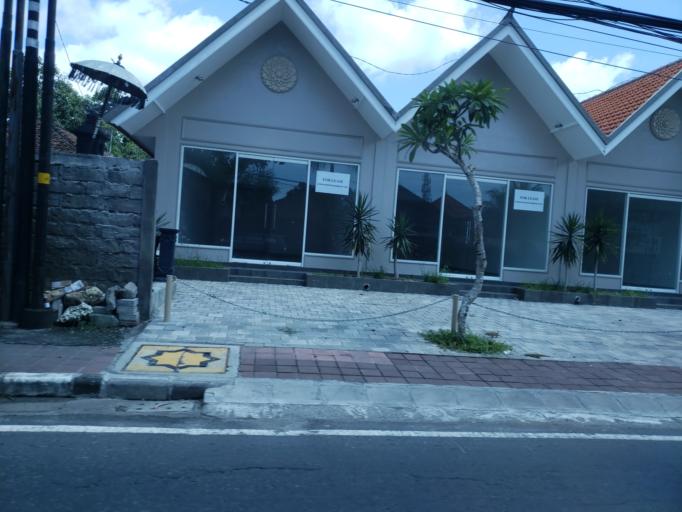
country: ID
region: Bali
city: Jimbaran
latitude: -8.7829
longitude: 115.1669
